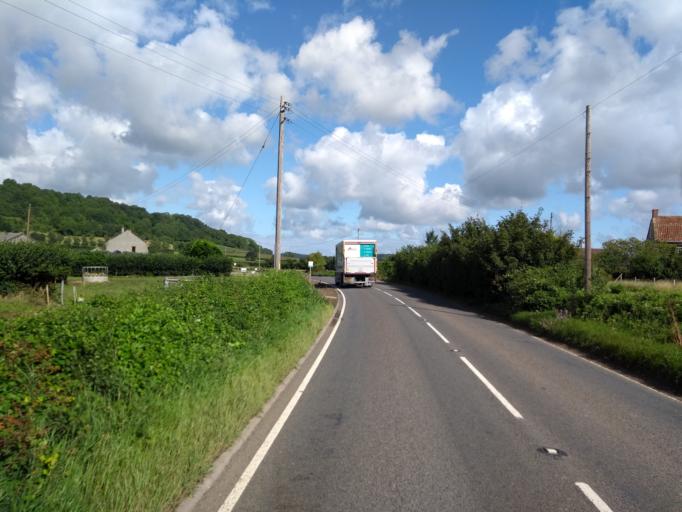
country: GB
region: England
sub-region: Somerset
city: Street
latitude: 51.0820
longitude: -2.7249
